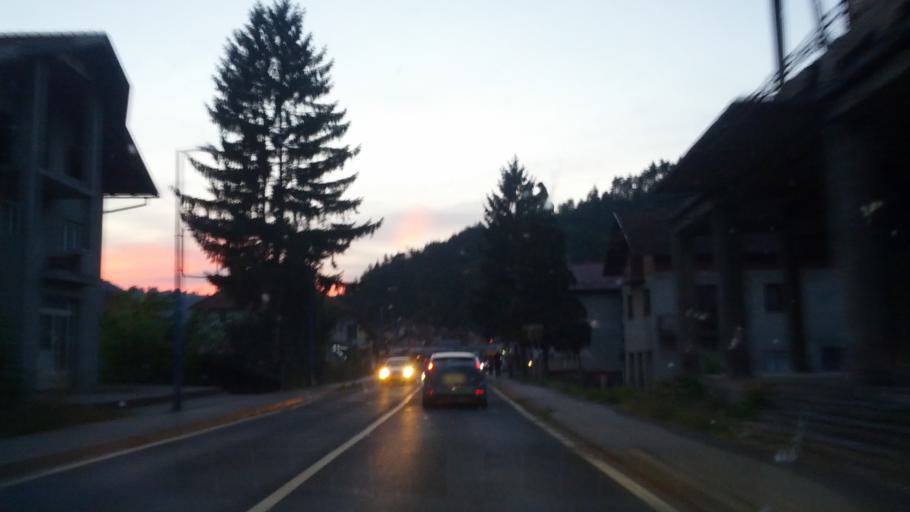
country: BA
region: Federation of Bosnia and Herzegovina
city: Bosanska Krupa
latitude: 44.8855
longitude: 16.1520
